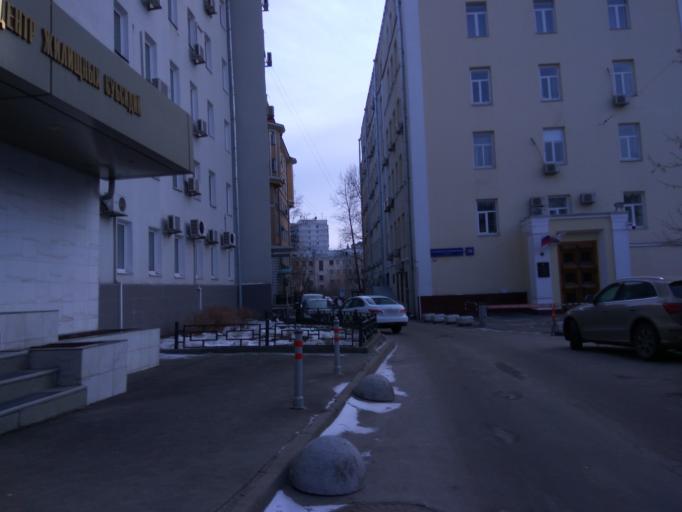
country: RU
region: Moscow
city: Moscow
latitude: 55.7730
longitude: 37.6281
